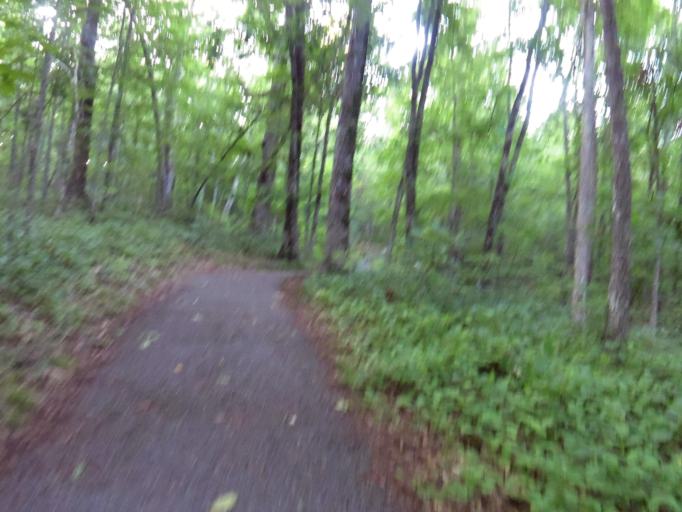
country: US
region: Tennessee
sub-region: Blount County
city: Maryville
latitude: 35.6320
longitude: -83.9410
